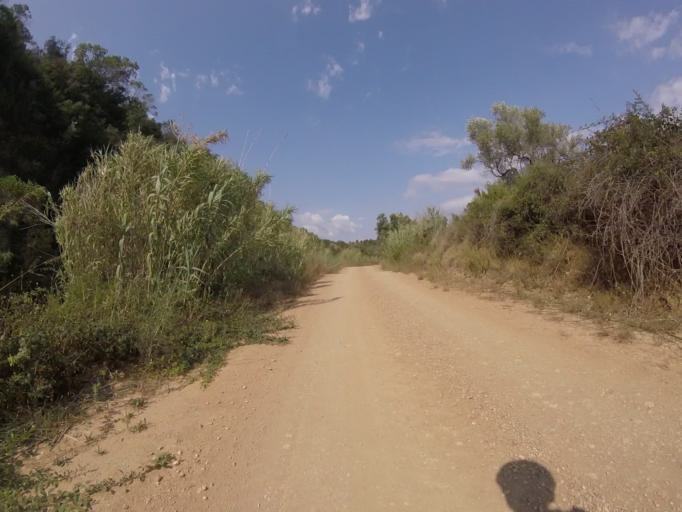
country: ES
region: Valencia
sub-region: Provincia de Castello
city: Alcala de Xivert
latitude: 40.3157
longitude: 0.1833
